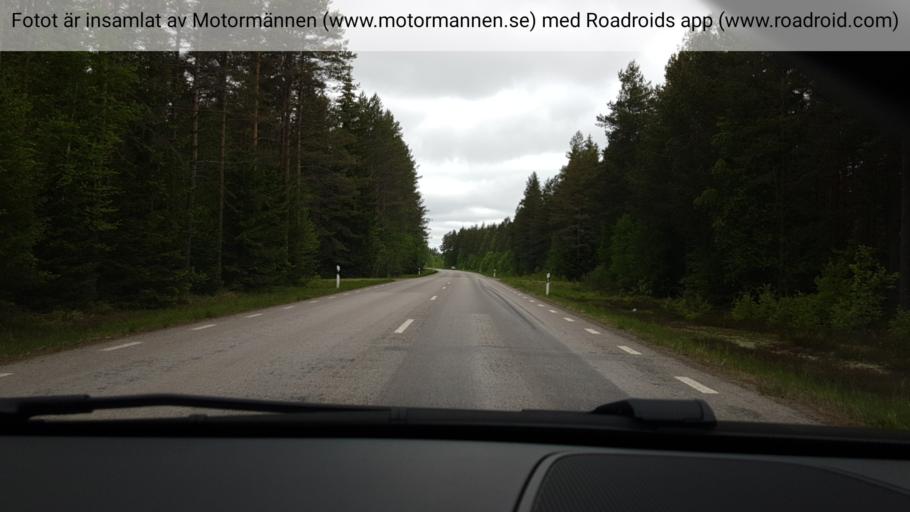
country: SE
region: Uppsala
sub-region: Tierps Kommun
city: Tierp
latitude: 60.3587
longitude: 17.4399
